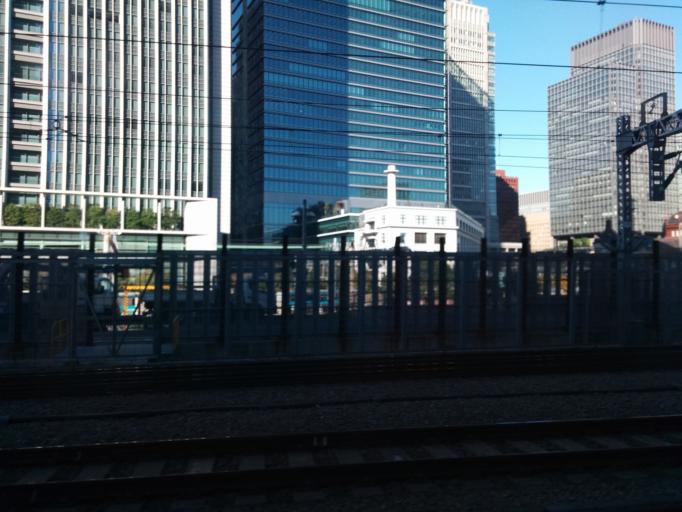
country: JP
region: Tokyo
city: Tokyo
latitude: 35.6783
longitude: 139.7665
